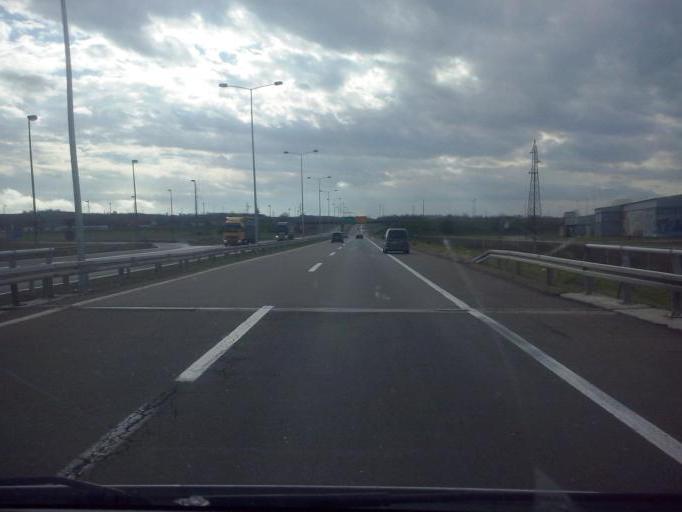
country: RS
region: Central Serbia
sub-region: Pomoravski Okrug
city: Paracin
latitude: 43.8605
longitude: 21.4375
